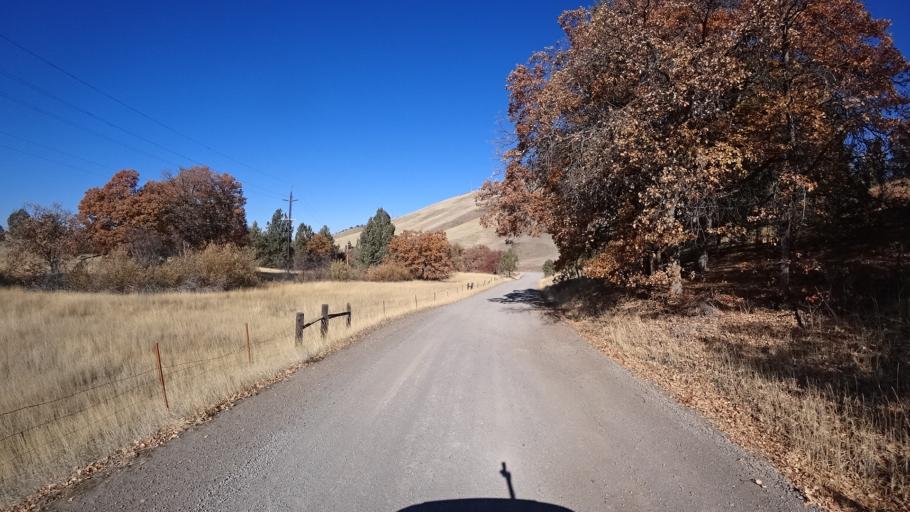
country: US
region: California
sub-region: Siskiyou County
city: Montague
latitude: 41.7919
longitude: -122.3612
